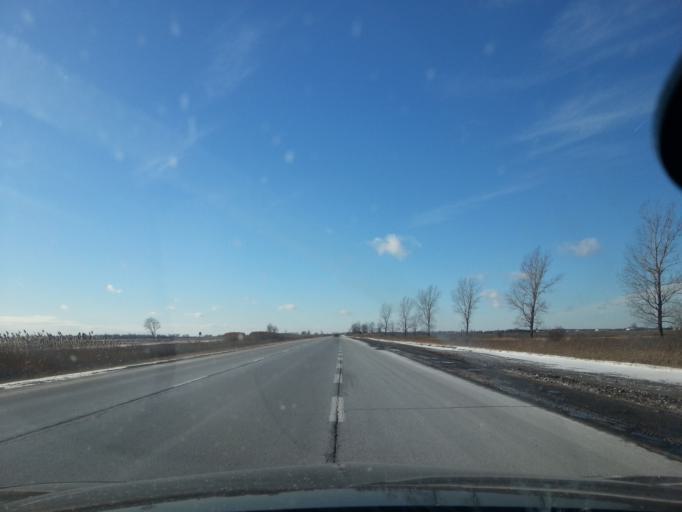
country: CA
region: Ontario
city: Casselman
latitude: 45.3261
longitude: -74.9860
